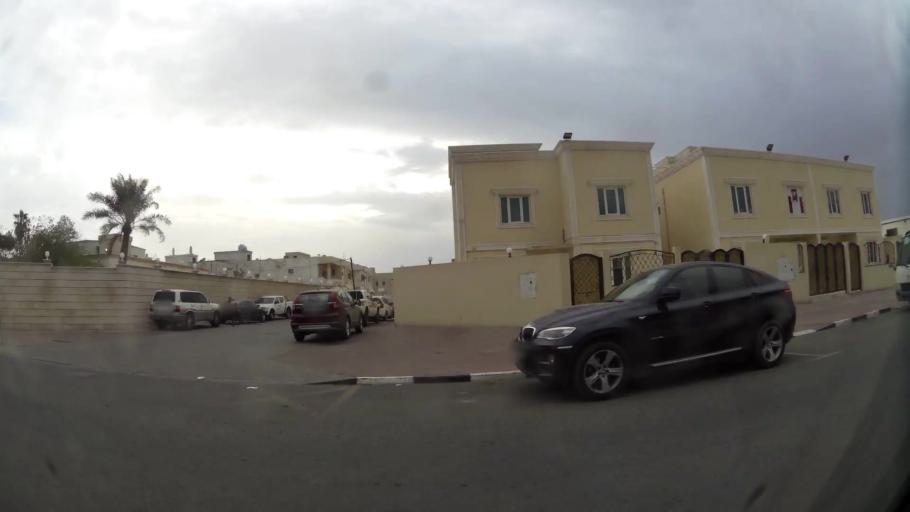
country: QA
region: Baladiyat ad Dawhah
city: Doha
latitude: 25.2720
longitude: 51.4950
